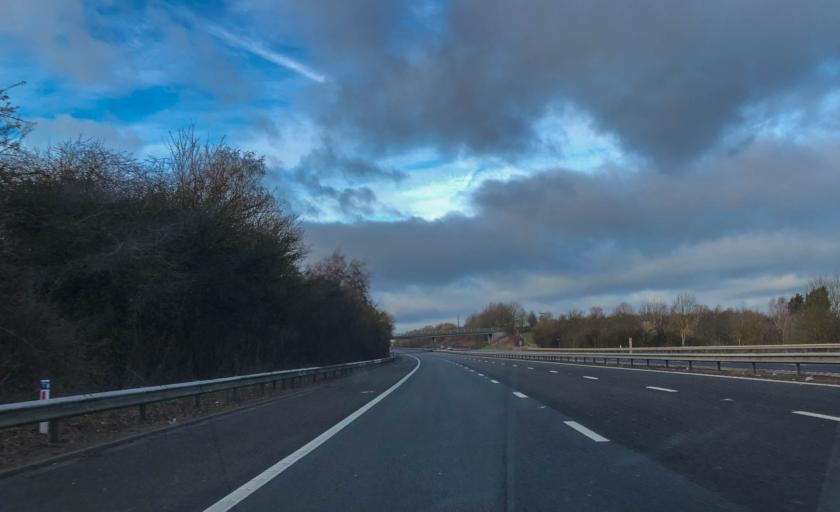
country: GB
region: England
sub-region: Kent
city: Longfield
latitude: 51.3607
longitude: 0.2682
